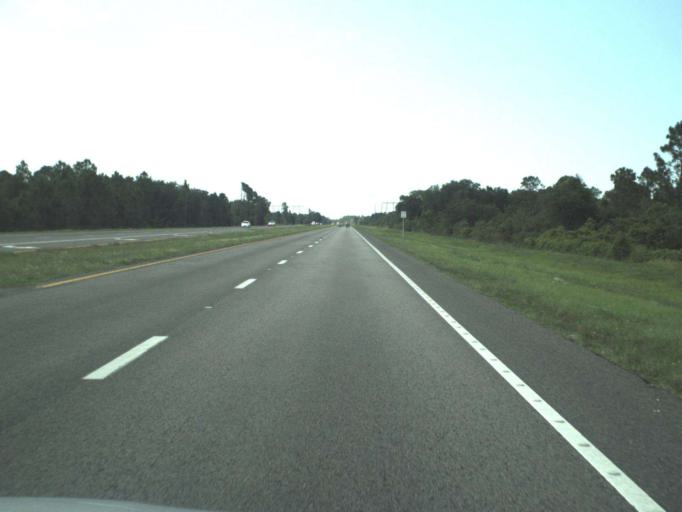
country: US
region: Florida
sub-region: Orange County
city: Christmas
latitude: 28.4008
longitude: -80.9469
